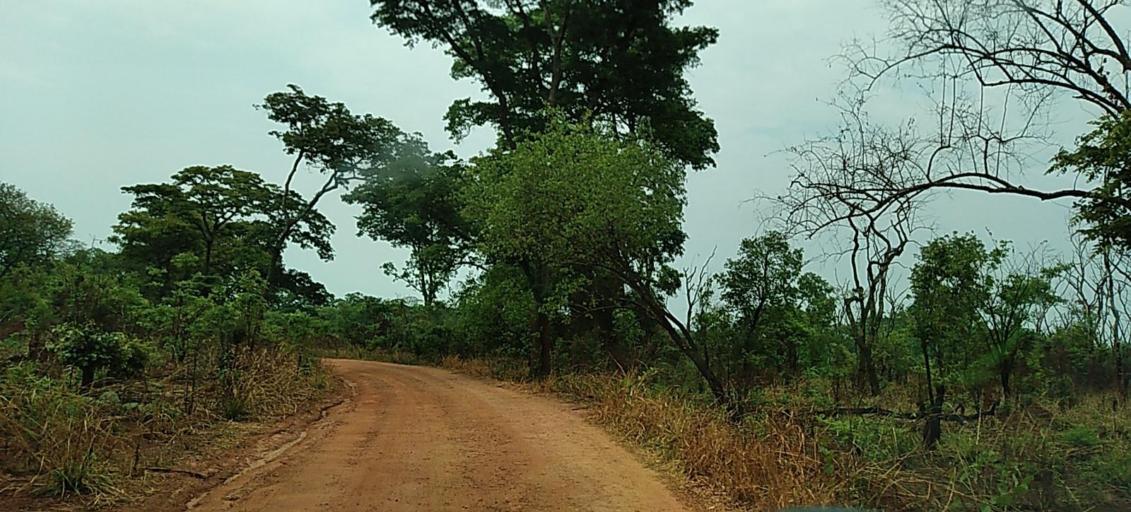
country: ZM
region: North-Western
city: Solwezi
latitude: -12.3293
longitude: 26.5203
